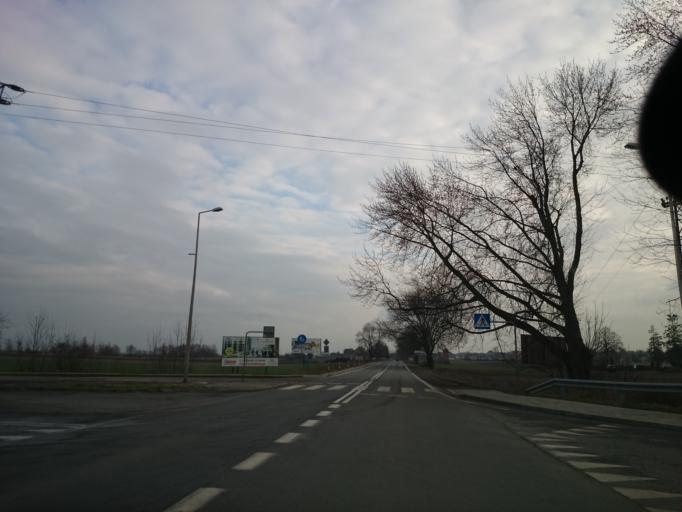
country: PL
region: Opole Voivodeship
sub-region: Powiat opolski
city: Opole
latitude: 50.6452
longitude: 17.9109
